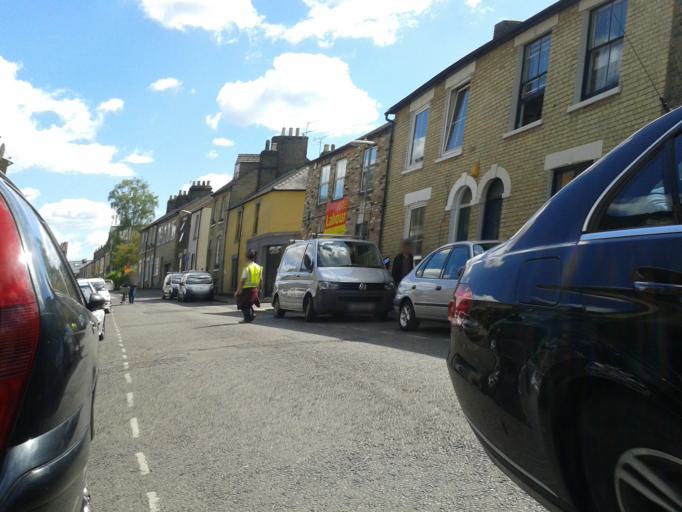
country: GB
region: England
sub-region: Cambridgeshire
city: Cambridge
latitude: 52.2046
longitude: 0.1369
